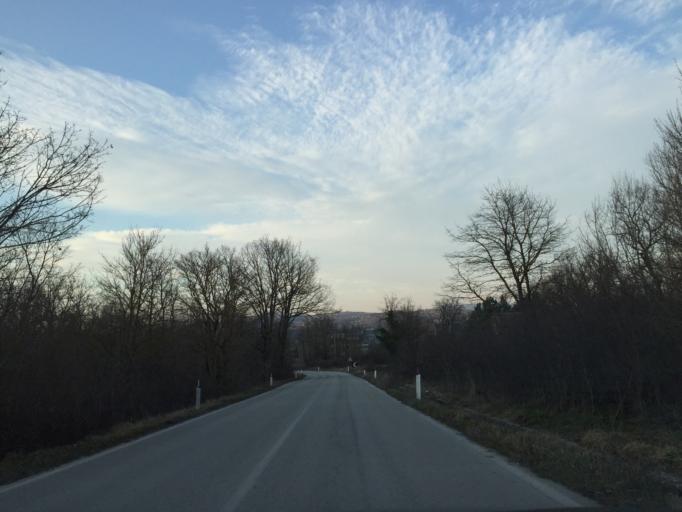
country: IT
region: Molise
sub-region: Provincia di Campobasso
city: Guardiaregia
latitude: 41.4528
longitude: 14.5564
